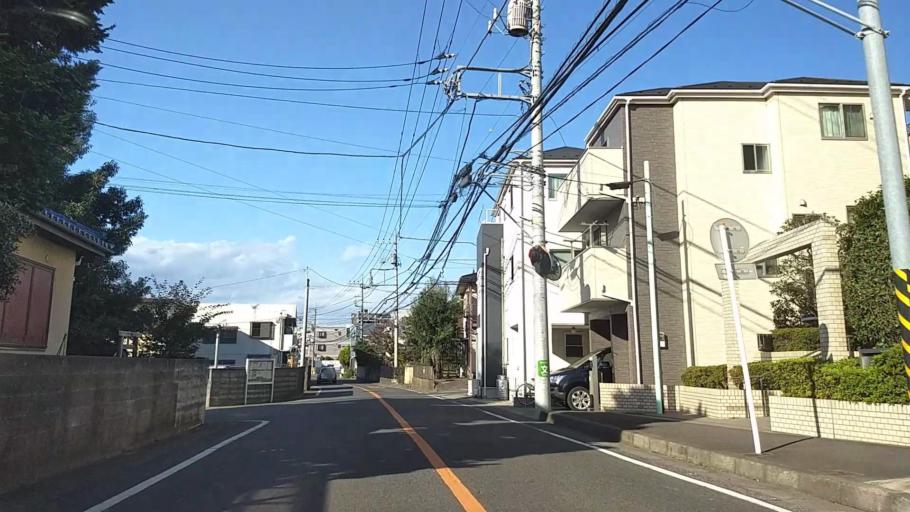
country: JP
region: Tokyo
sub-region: Machida-shi
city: Machida
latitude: 35.5393
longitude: 139.5439
